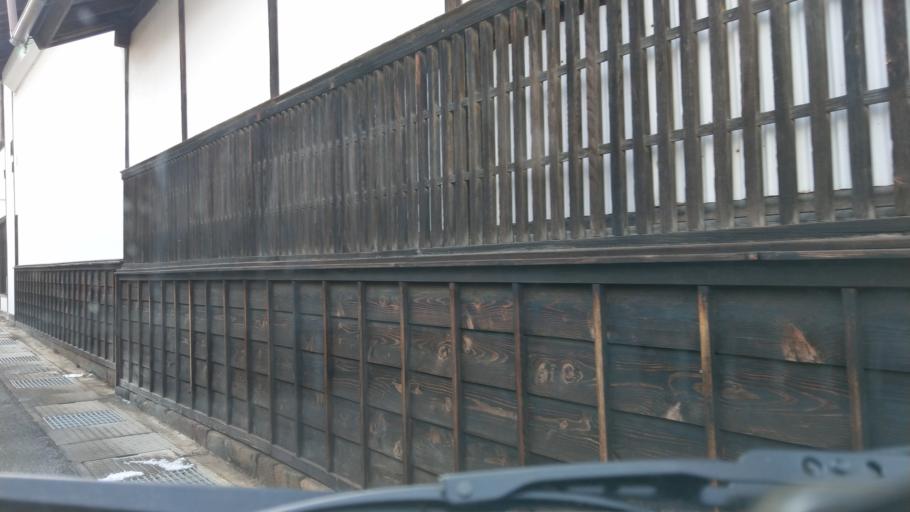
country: JP
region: Nagano
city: Kamimaruko
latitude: 36.2710
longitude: 138.3336
